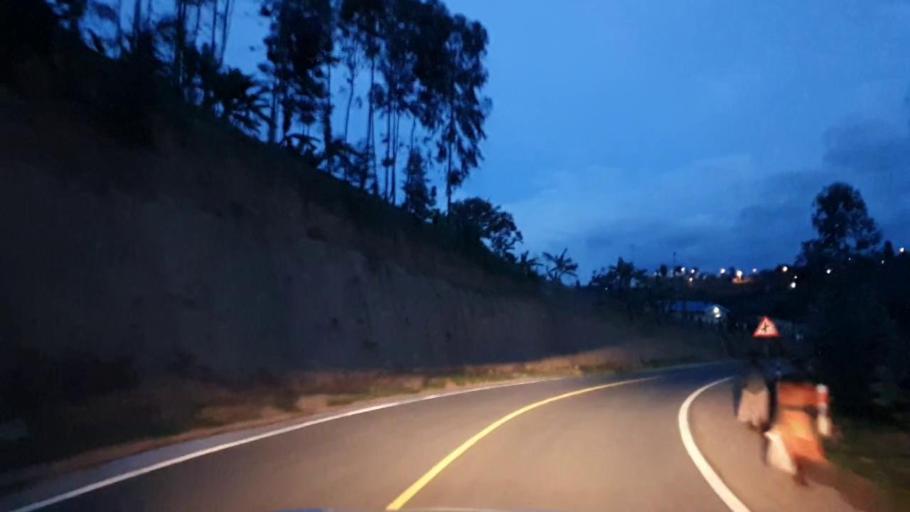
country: RW
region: Southern Province
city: Gikongoro
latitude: -2.4644
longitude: 29.5666
